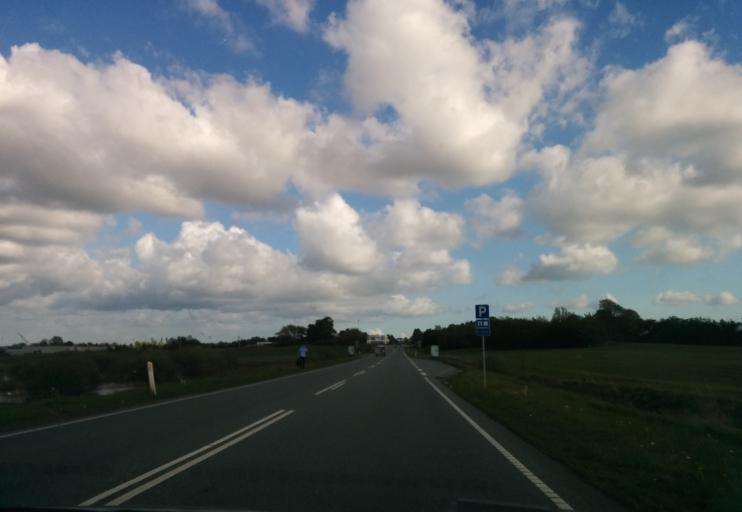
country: DK
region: Central Jutland
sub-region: Arhus Kommune
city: Stavtrup
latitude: 56.1136
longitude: 10.1138
